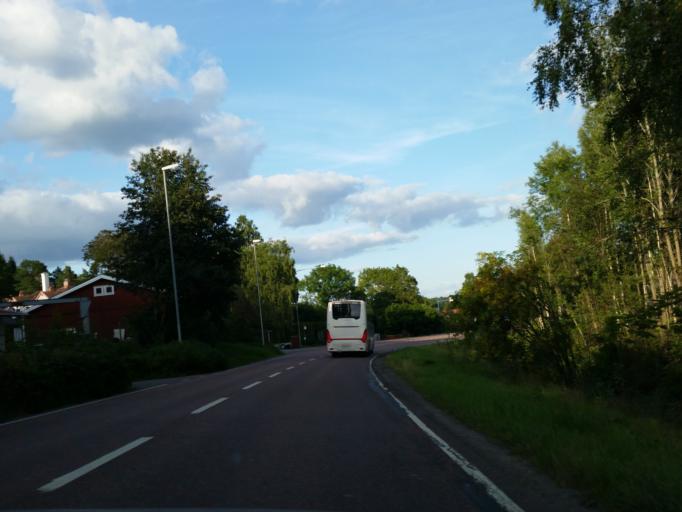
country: SE
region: Stockholm
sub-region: Sodertalje Kommun
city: Pershagen
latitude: 59.0884
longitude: 17.5713
